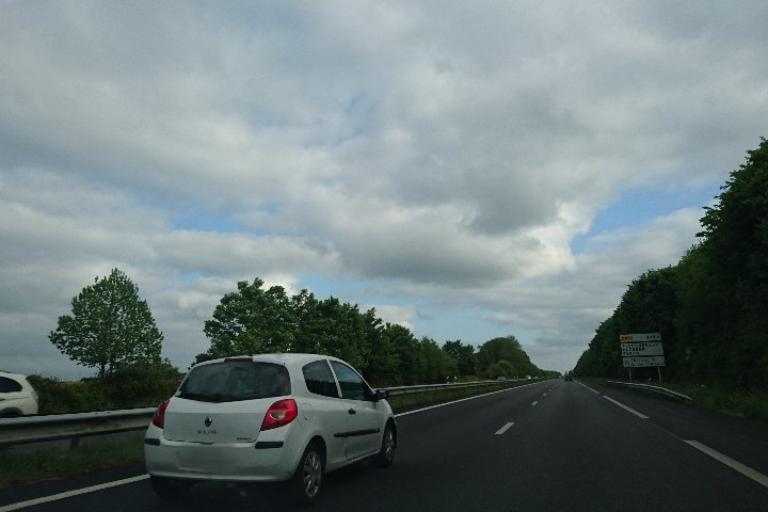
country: FR
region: Brittany
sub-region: Departement d'Ille-et-Vilaine
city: Pleugueneuc
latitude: 48.4173
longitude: -1.9096
